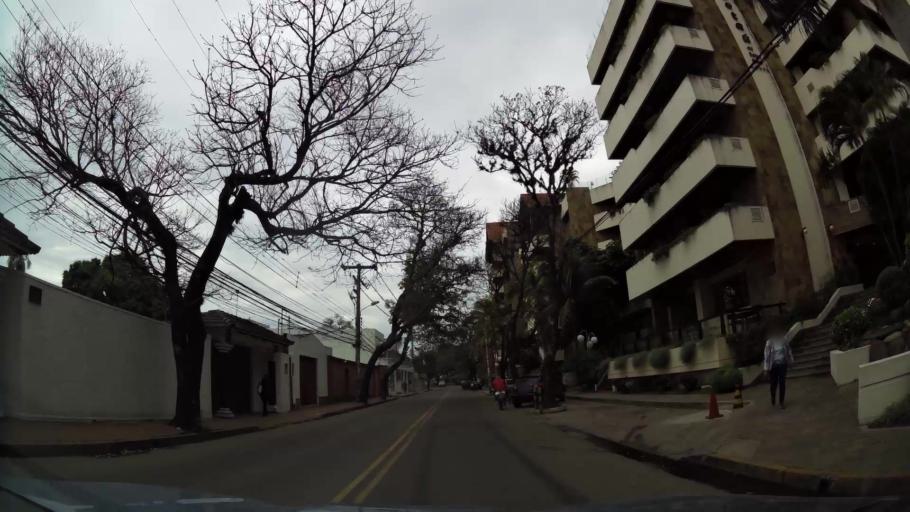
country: BO
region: Santa Cruz
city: Santa Cruz de la Sierra
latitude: -17.7713
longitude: -63.1913
